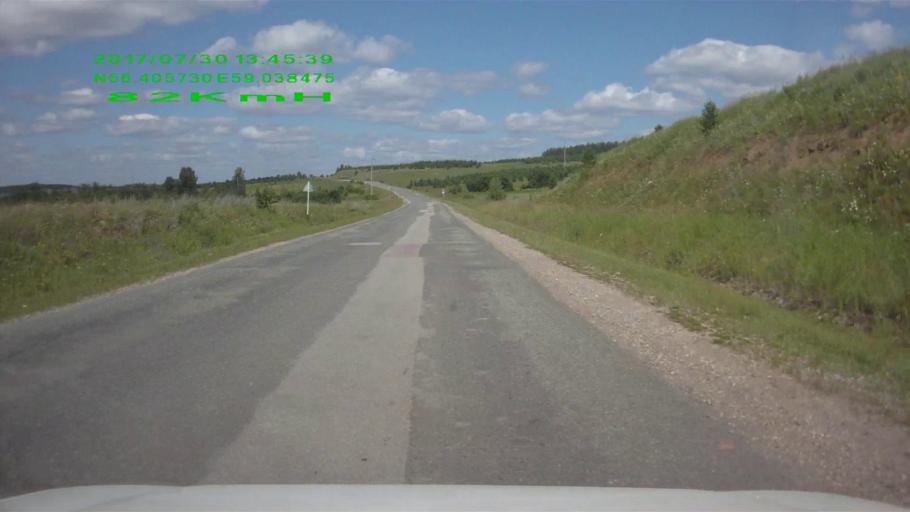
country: RU
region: Sverdlovsk
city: Mikhaylovsk
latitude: 56.4062
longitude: 59.0392
